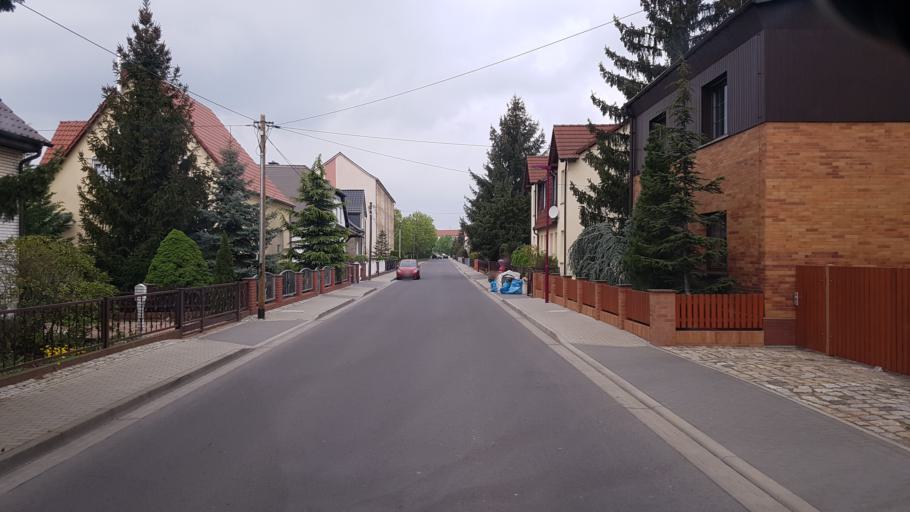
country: DE
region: Brandenburg
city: Grossraschen
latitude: 51.5874
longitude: 14.0031
